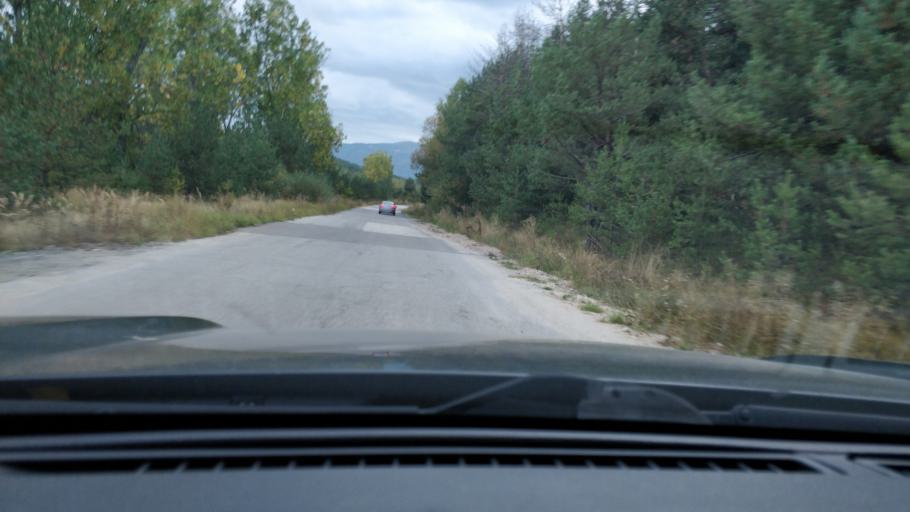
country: BG
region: Sofiya
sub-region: Obshtina Samokov
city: Samokov
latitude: 42.4808
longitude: 23.3953
